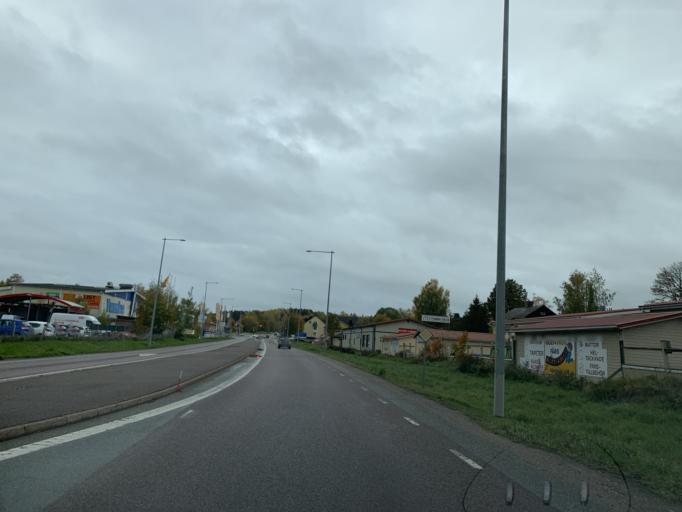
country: SE
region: Stockholm
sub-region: Botkyrka Kommun
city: Tumba
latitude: 59.1922
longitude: 17.8241
